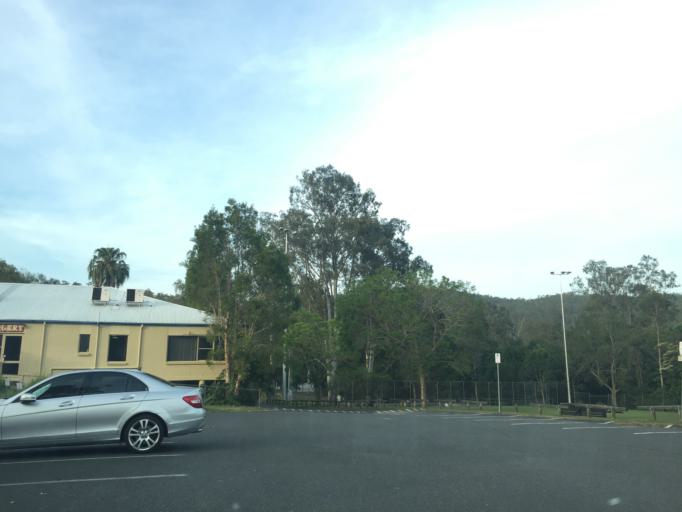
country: AU
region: Queensland
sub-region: Brisbane
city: Taringa
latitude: -27.4468
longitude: 152.9538
